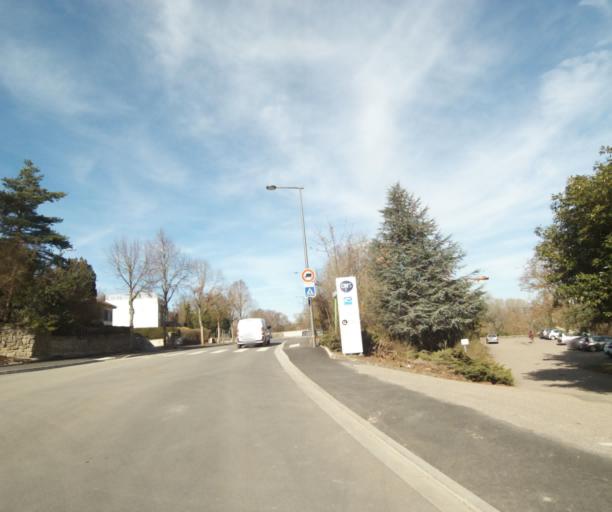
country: FR
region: Lorraine
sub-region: Departement de Meurthe-et-Moselle
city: Villers-les-Nancy
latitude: 48.6642
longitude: 6.1524
